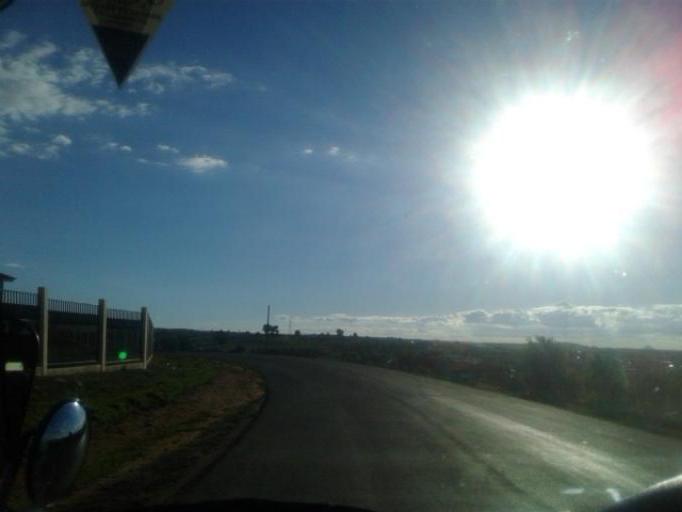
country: LS
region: Maseru
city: Maseru
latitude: -29.3183
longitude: 27.5853
